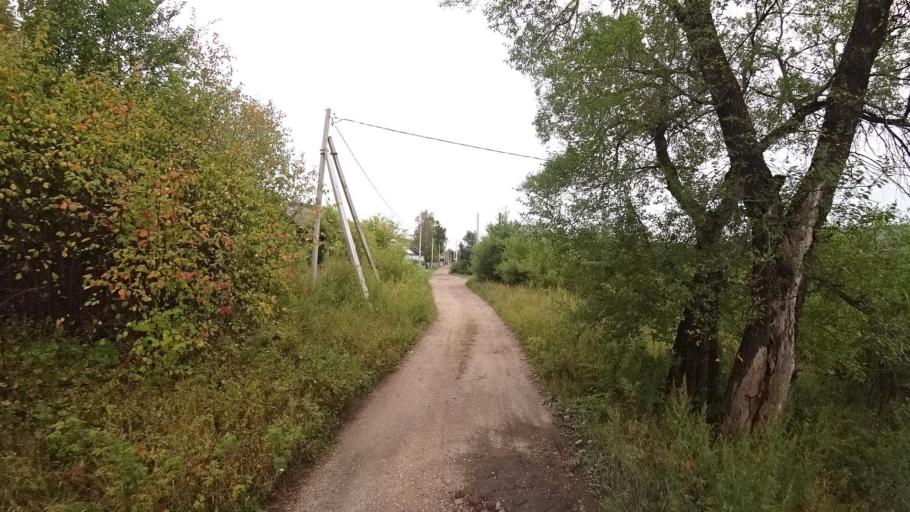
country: RU
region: Jewish Autonomous Oblast
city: Khingansk
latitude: 49.0360
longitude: 131.0604
